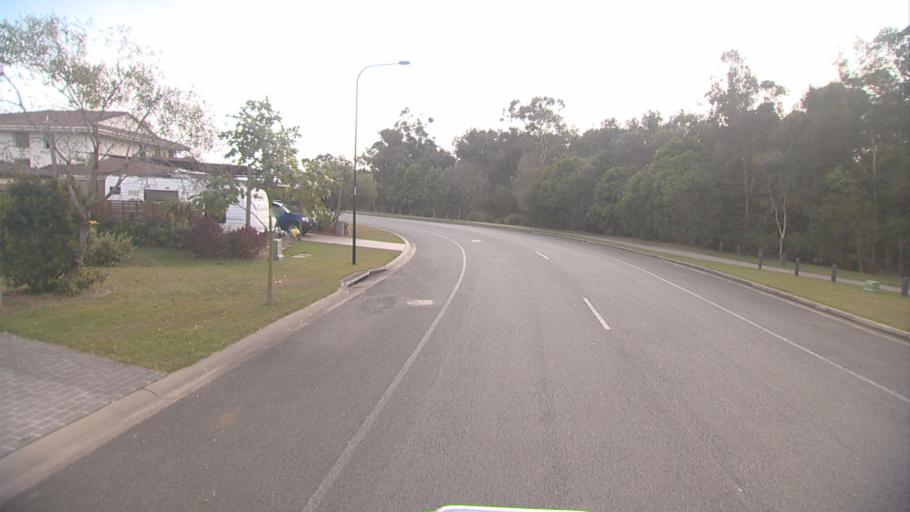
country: AU
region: Queensland
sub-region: Logan
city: Woodridge
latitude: -27.6570
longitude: 153.0756
